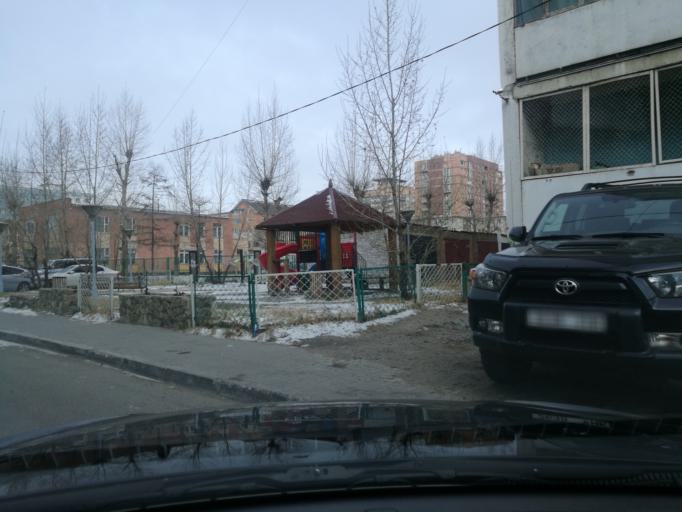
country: MN
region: Ulaanbaatar
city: Ulaanbaatar
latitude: 47.9106
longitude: 106.9023
